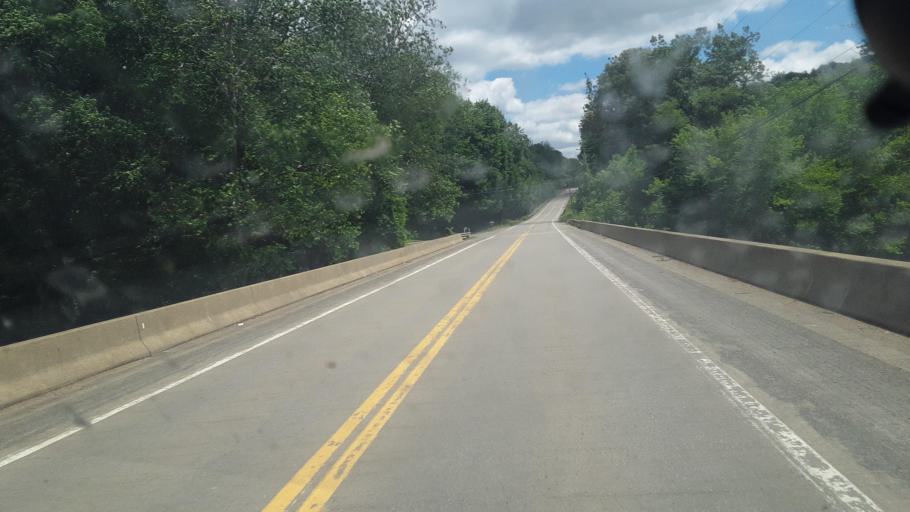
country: US
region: Pennsylvania
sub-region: Butler County
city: Slippery Rock
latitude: 41.0119
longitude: -80.1782
